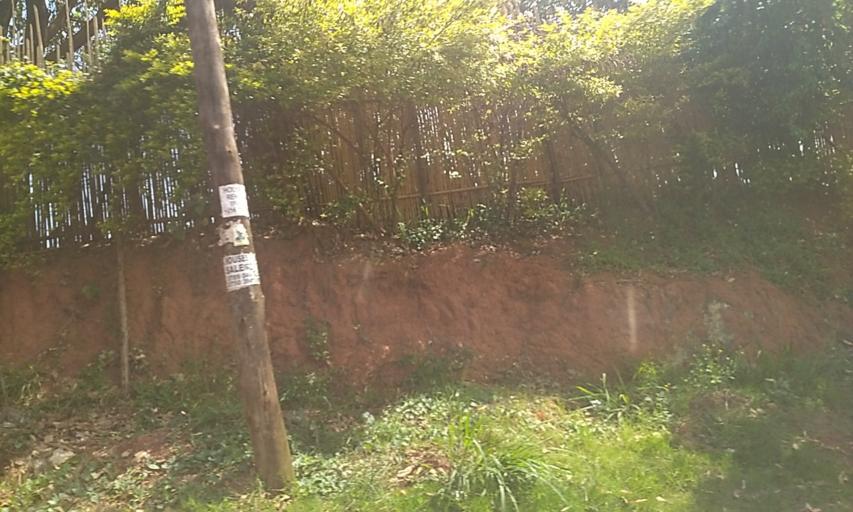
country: UG
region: Central Region
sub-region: Wakiso District
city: Kireka
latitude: 0.3521
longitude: 32.6112
